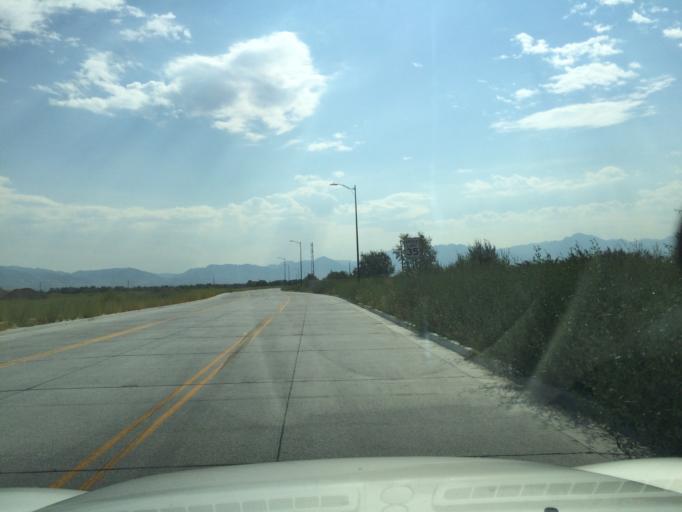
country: US
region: Utah
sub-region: Salt Lake County
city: Magna
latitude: 40.7149
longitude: -112.0524
